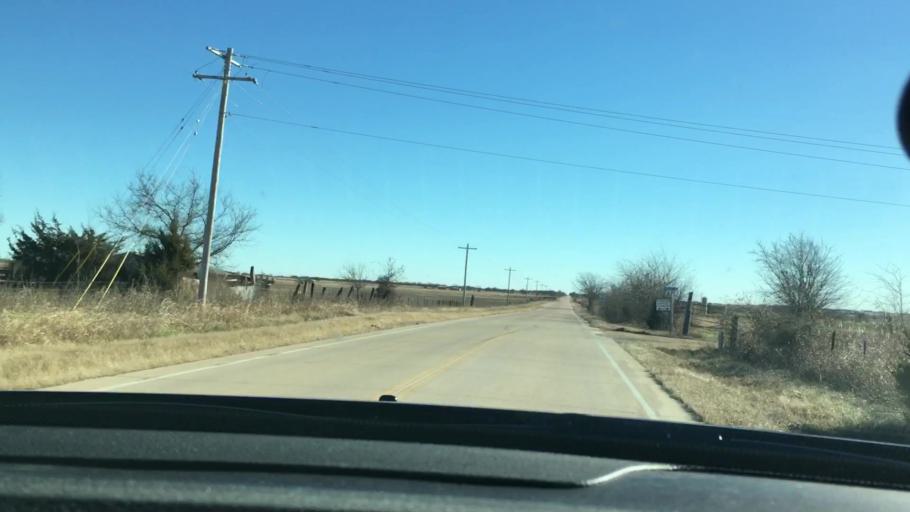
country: US
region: Oklahoma
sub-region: Marshall County
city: Madill
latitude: 34.1144
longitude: -96.7064
